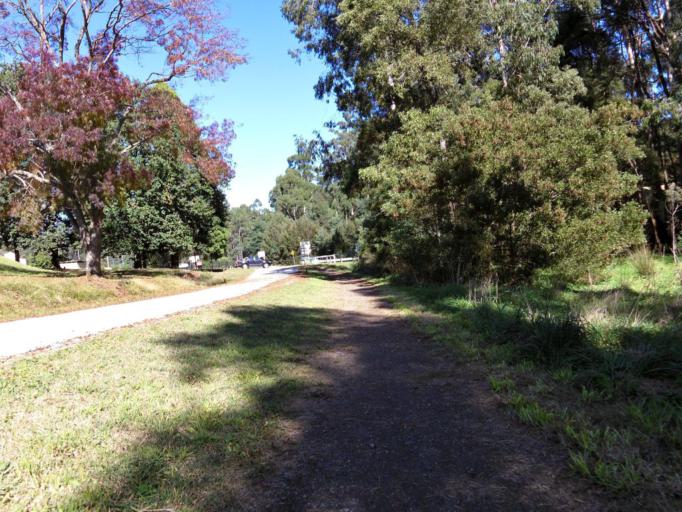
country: AU
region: Victoria
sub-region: Cardinia
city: Cockatoo
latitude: -37.9349
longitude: 145.4903
